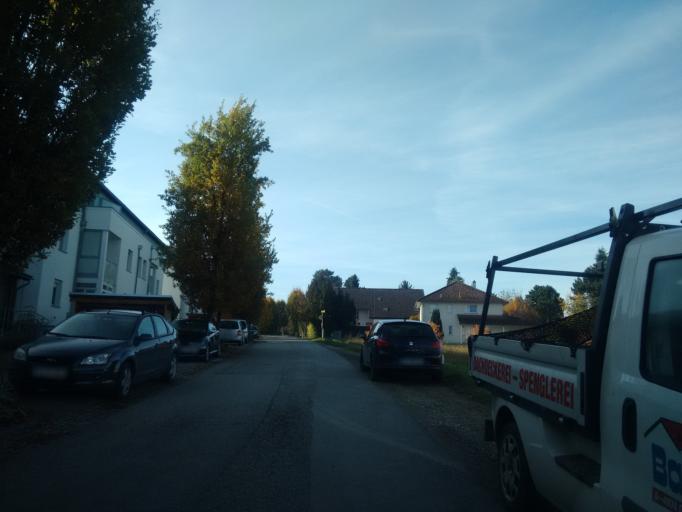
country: AT
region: Upper Austria
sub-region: Politischer Bezirk Ried im Innkreis
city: Ried im Innkreis
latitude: 48.2148
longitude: 13.4975
